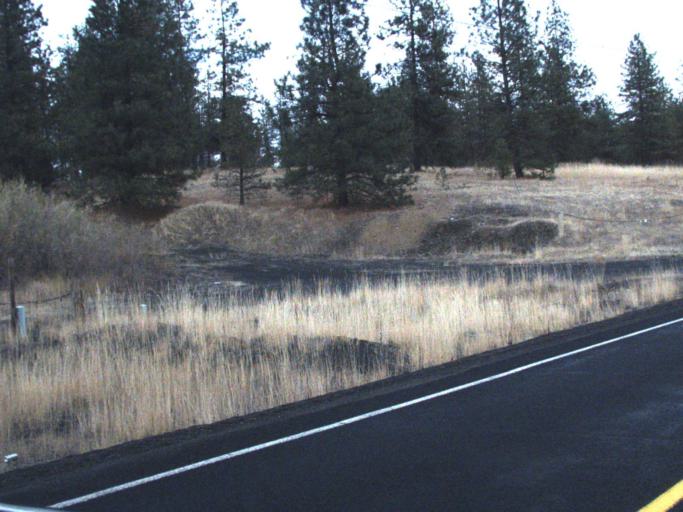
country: US
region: Washington
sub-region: Lincoln County
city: Davenport
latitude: 47.8234
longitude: -118.1885
